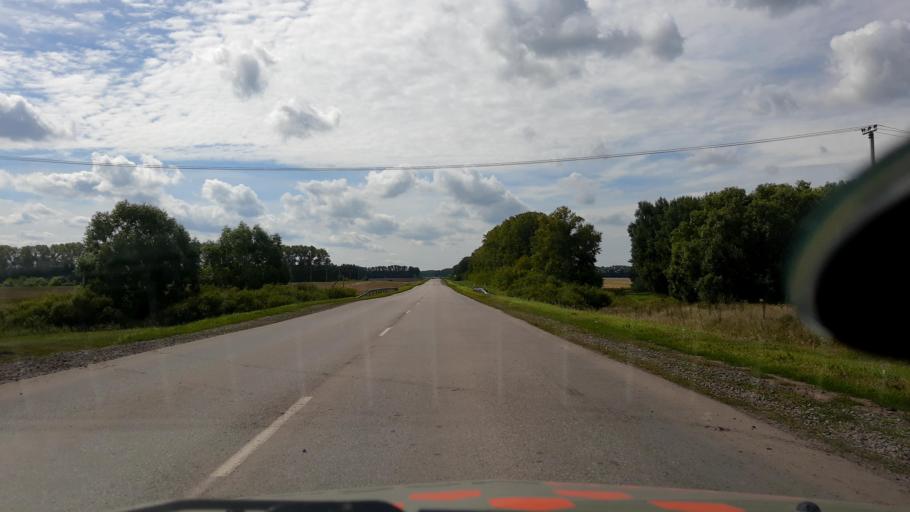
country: RU
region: Bashkortostan
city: Buzdyak
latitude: 54.6818
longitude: 54.5522
